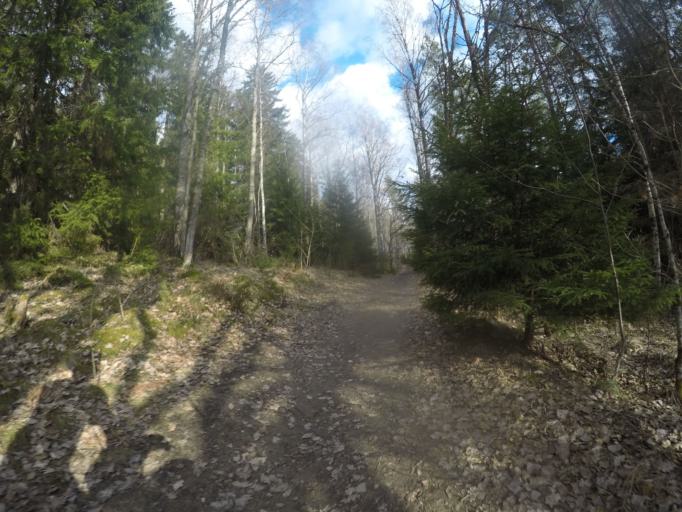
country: SE
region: Soedermanland
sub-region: Eskilstuna Kommun
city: Hallbybrunn
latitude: 59.3885
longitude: 16.3901
